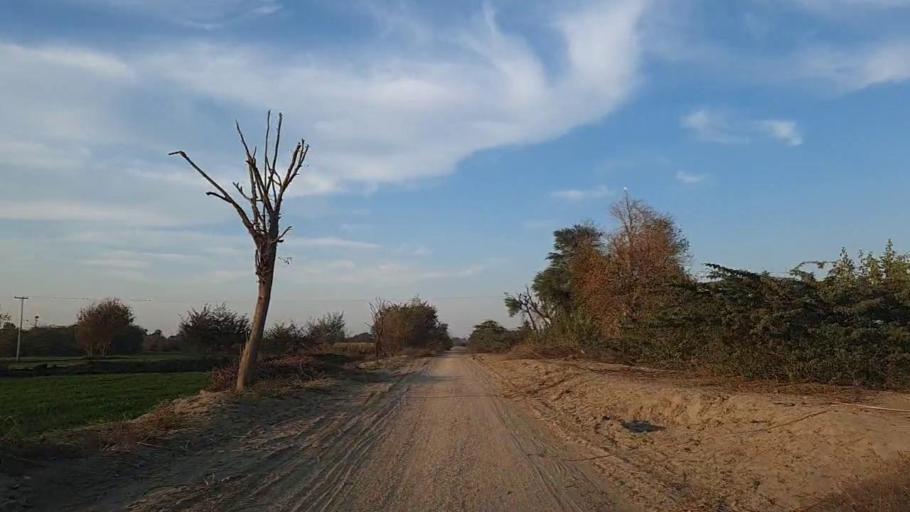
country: PK
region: Sindh
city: Bandhi
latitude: 26.5993
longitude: 68.3590
